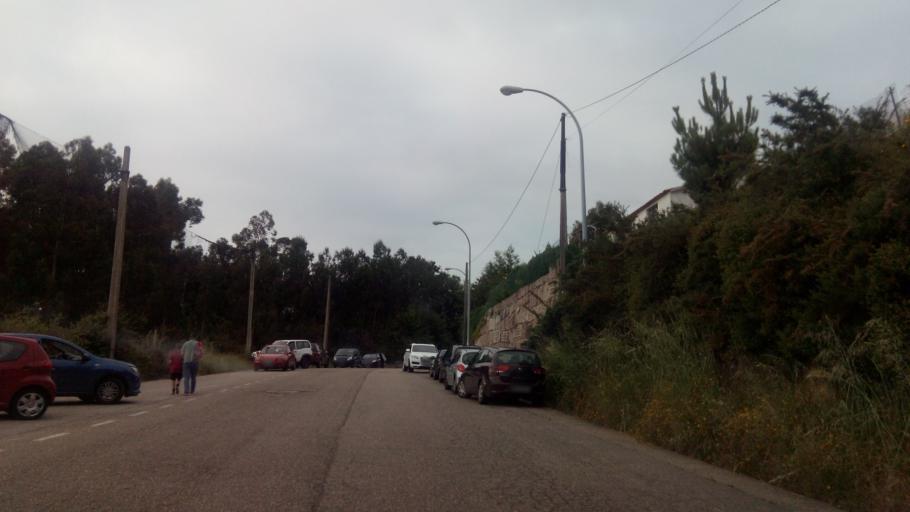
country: ES
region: Galicia
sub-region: Provincia de Pontevedra
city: Nigran
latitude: 42.1203
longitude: -8.8012
